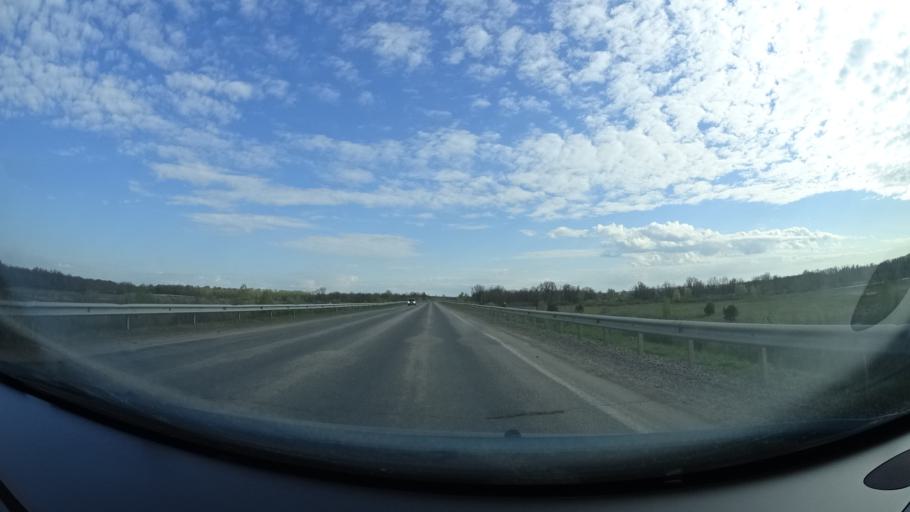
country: RU
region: Bashkortostan
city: Blagoveshchensk
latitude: 55.0115
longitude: 55.7837
